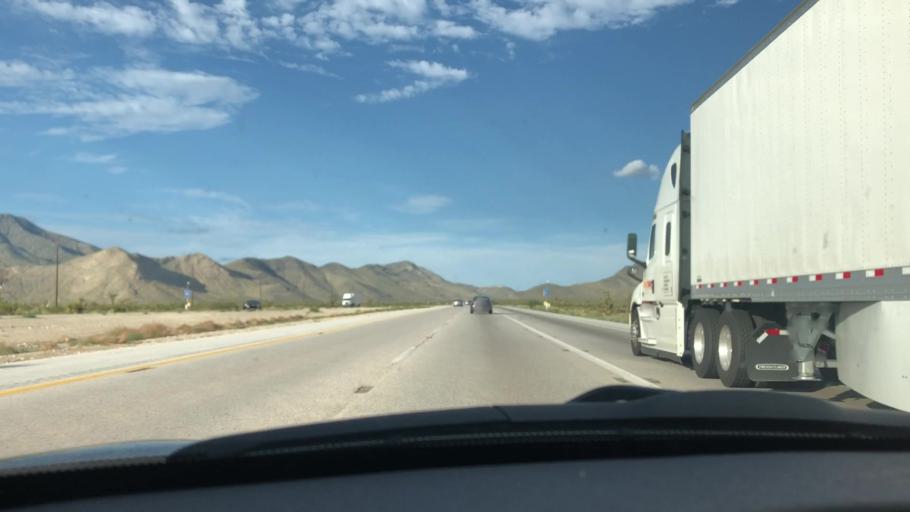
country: US
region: Nevada
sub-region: Clark County
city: Sandy Valley
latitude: 35.4591
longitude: -115.6311
